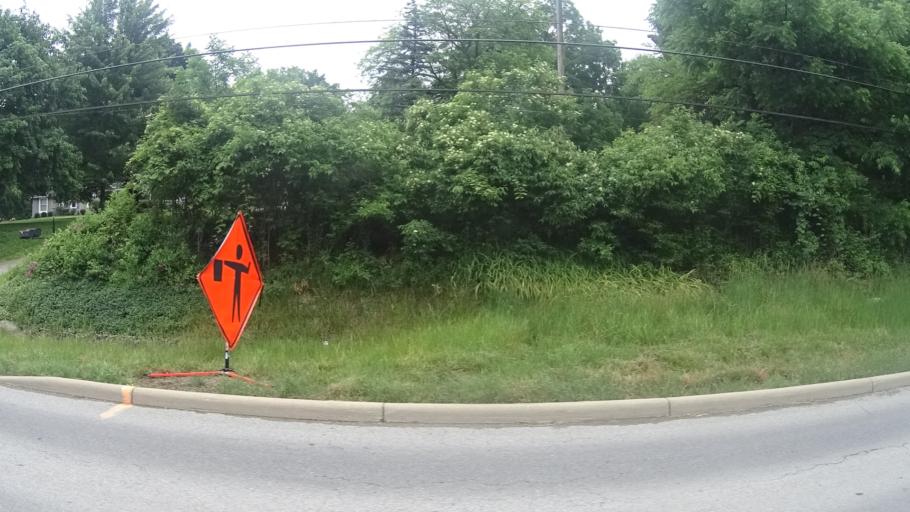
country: US
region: Ohio
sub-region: Erie County
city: Huron
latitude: 41.3299
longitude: -82.4935
